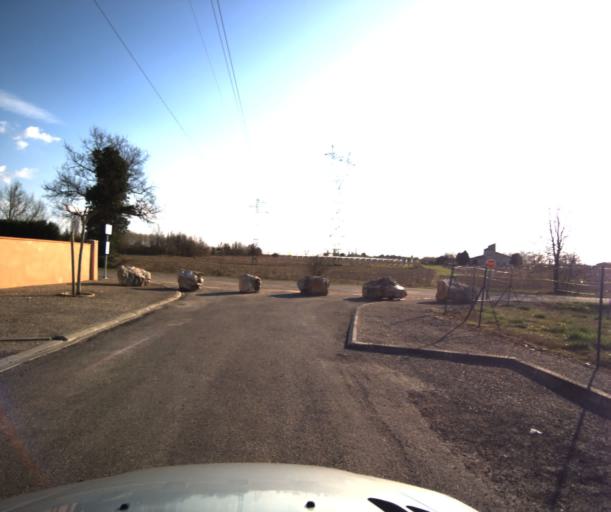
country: FR
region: Midi-Pyrenees
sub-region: Departement du Tarn-et-Garonne
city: Bressols
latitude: 43.9622
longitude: 1.3258
